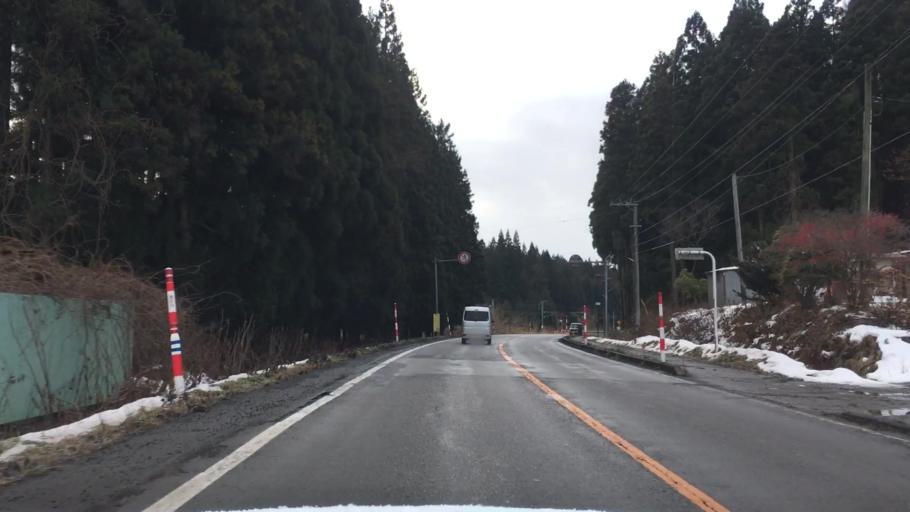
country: JP
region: Akita
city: Odate
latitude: 40.3273
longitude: 140.5828
